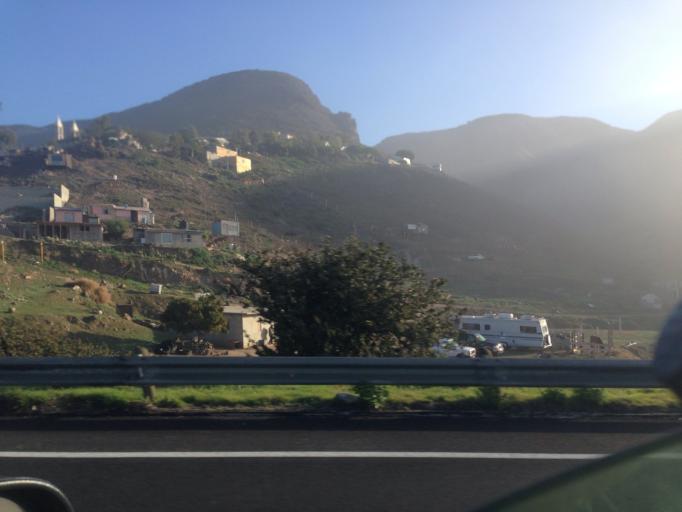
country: MX
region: Baja California
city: Primo Tapia
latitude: 32.1634
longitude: -116.8985
